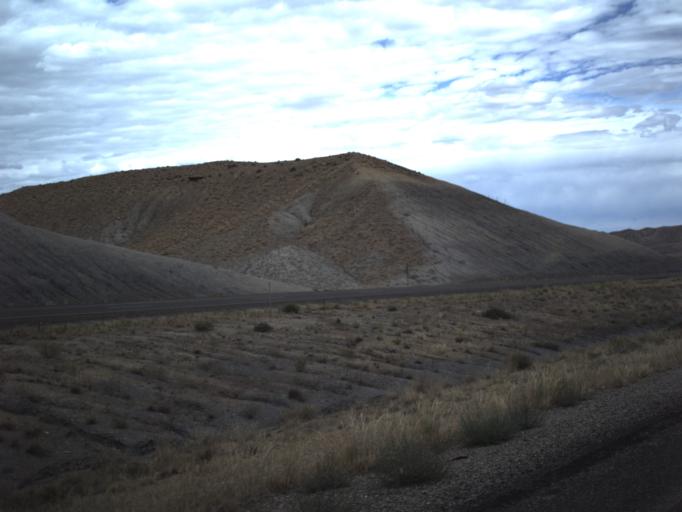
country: US
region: Utah
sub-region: Grand County
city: Moab
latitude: 38.9598
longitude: -109.7130
